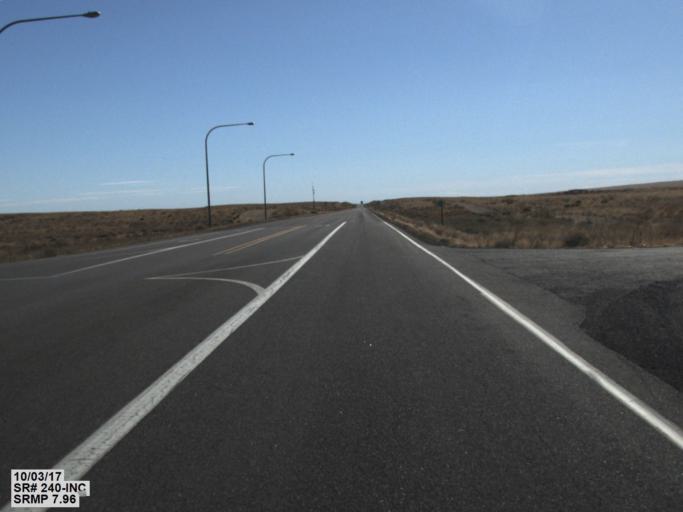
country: US
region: Washington
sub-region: Benton County
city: Benton City
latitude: 46.5023
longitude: -119.6164
